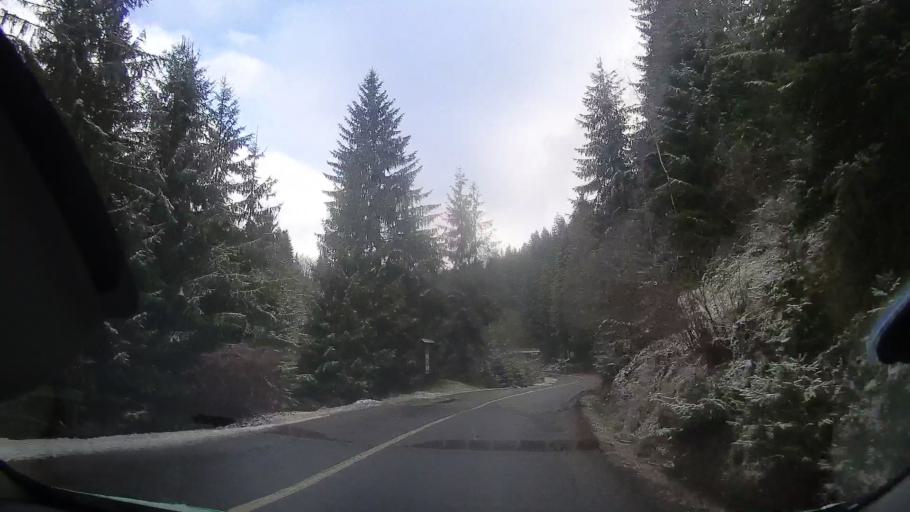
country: RO
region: Alba
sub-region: Comuna Horea
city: Horea
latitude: 46.4902
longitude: 22.9615
